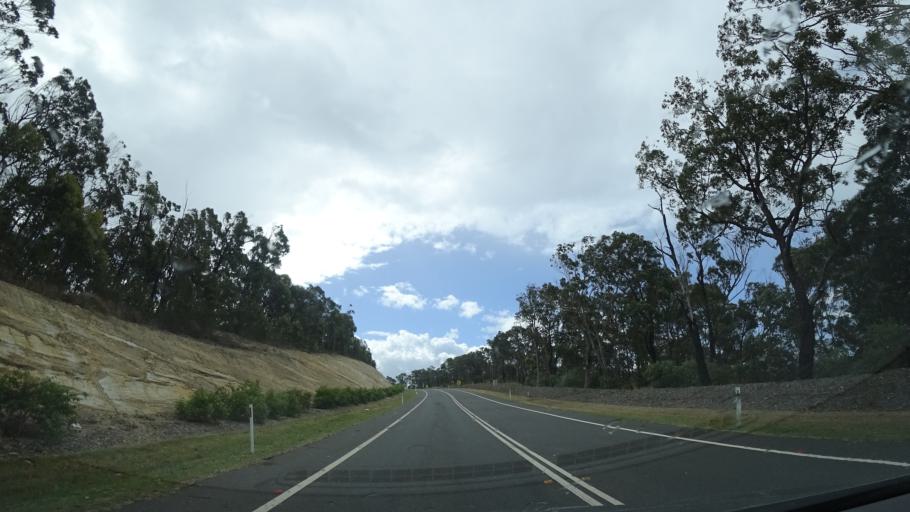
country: AU
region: New South Wales
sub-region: Wyong Shire
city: Kingfisher Shores
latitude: -33.1610
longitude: 151.6159
